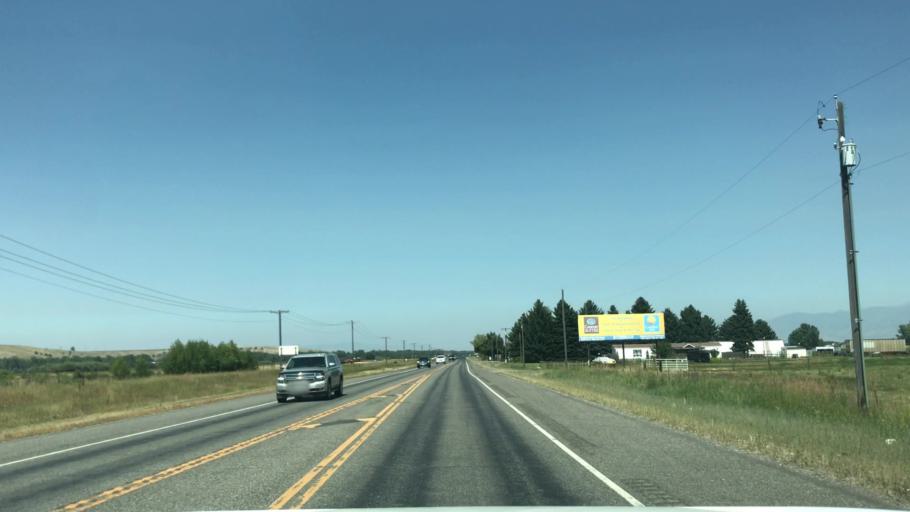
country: US
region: Montana
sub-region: Gallatin County
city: Four Corners
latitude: 45.6243
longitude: -111.1969
